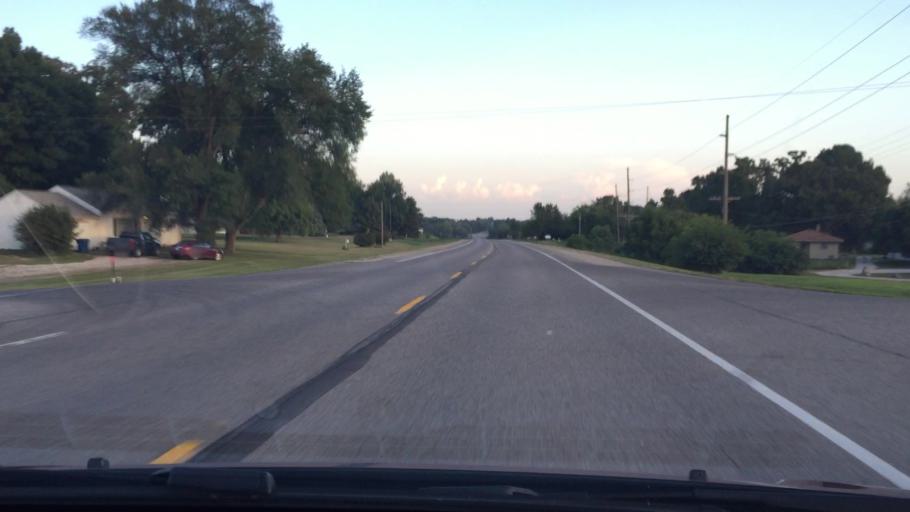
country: US
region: Iowa
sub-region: Muscatine County
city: Muscatine
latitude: 41.4702
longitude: -91.0366
